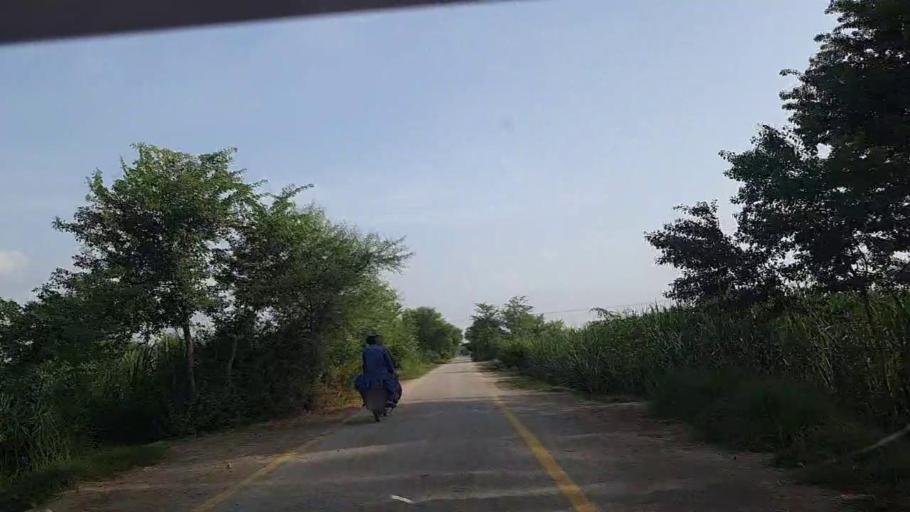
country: PK
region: Sindh
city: Ghotki
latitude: 27.9733
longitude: 69.2559
